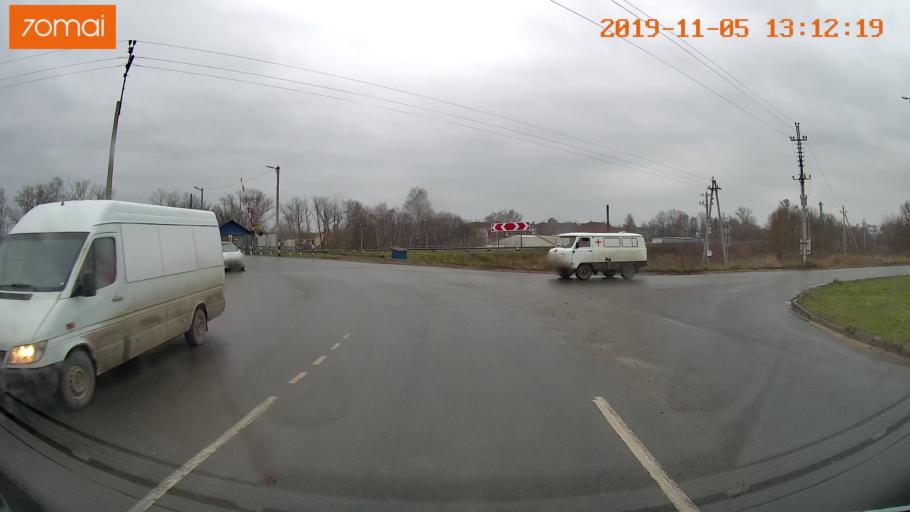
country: RU
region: Ivanovo
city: Shuya
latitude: 56.8569
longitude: 41.3506
